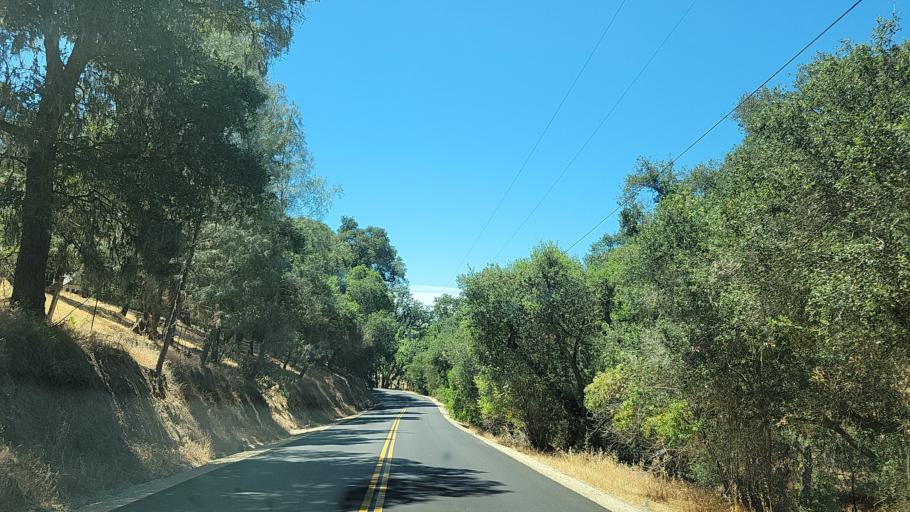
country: US
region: California
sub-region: San Luis Obispo County
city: Atascadero
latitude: 35.4802
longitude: -120.6265
